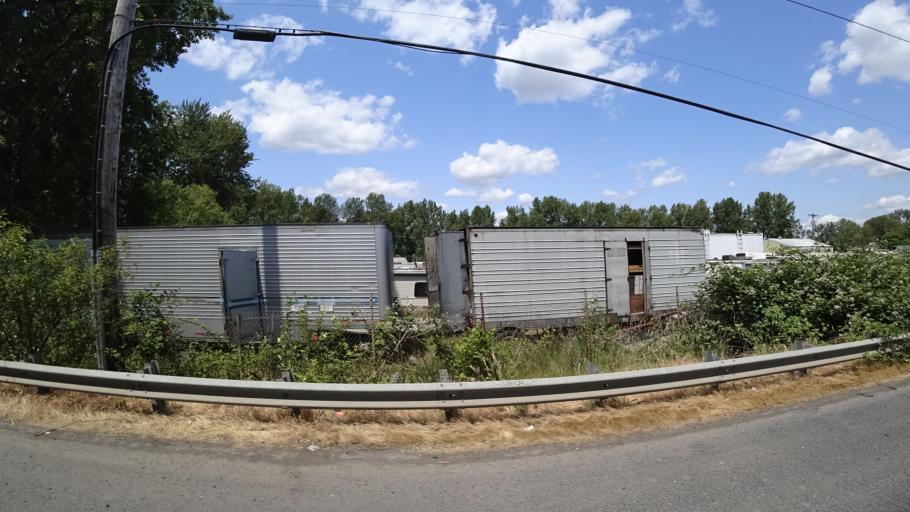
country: US
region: Washington
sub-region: Clark County
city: Vancouver
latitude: 45.6099
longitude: -122.7080
